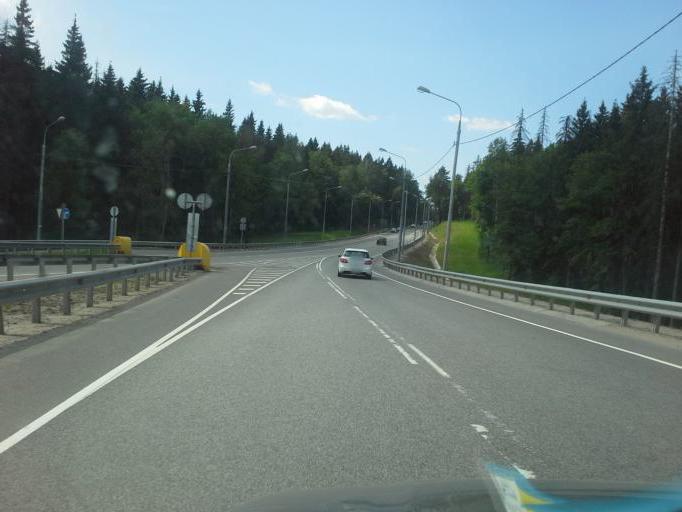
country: RU
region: Moskovskaya
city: Odintsovo
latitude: 55.6905
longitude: 37.2429
